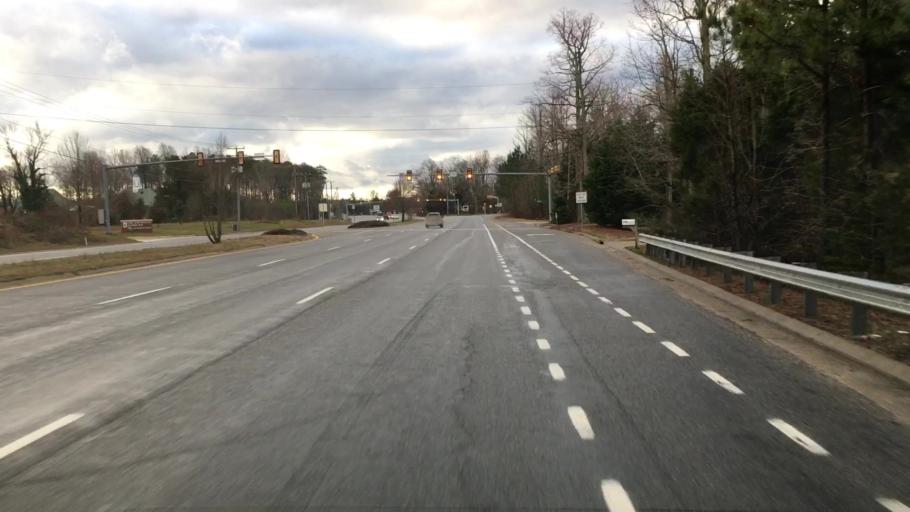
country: US
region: Virginia
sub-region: Chesterfield County
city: Bon Air
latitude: 37.4876
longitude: -77.5970
